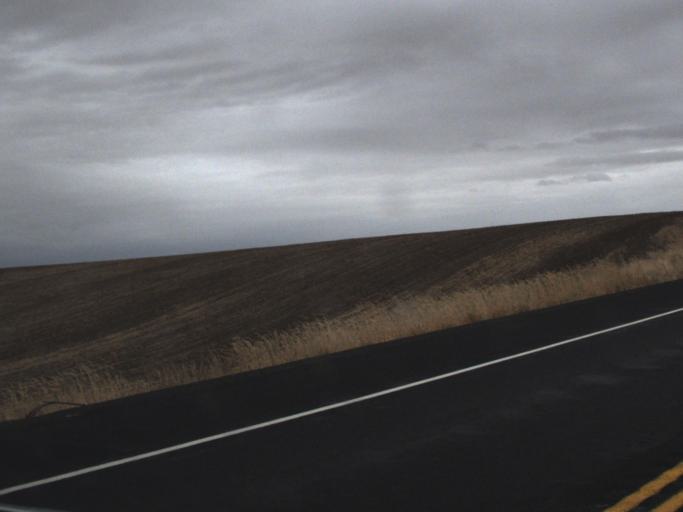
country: US
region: Washington
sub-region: Whitman County
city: Pullman
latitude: 46.6396
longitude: -117.1800
